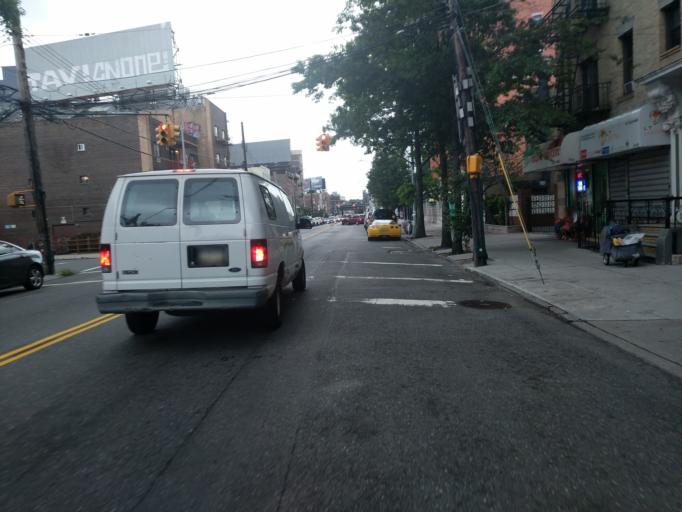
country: US
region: New York
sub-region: Queens County
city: Long Island City
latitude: 40.7709
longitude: -73.9217
